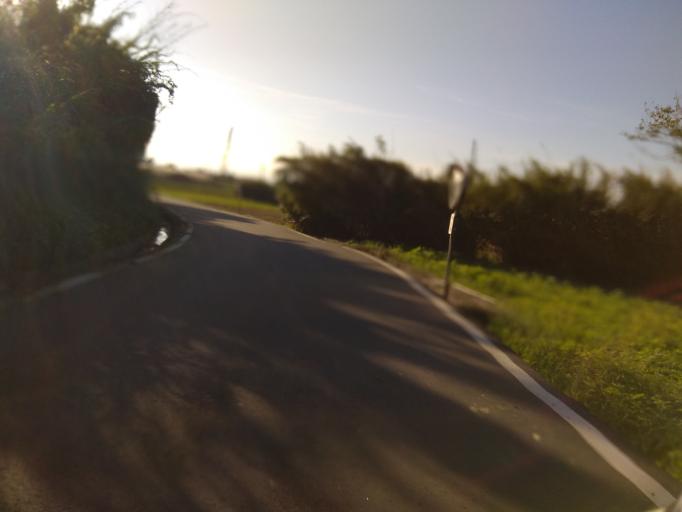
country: TW
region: Taiwan
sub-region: Hsinchu
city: Zhubei
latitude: 24.9927
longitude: 121.0561
